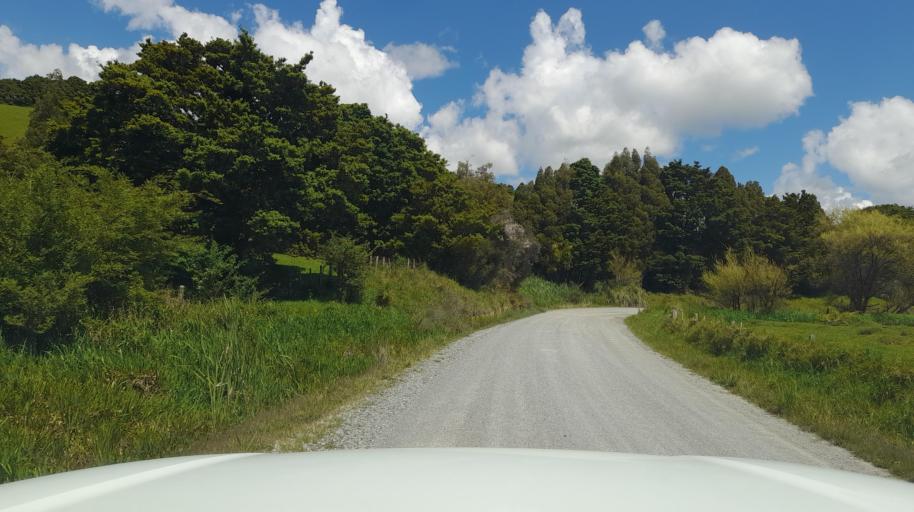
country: NZ
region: Northland
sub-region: Far North District
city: Kaitaia
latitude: -35.1159
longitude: 173.3947
